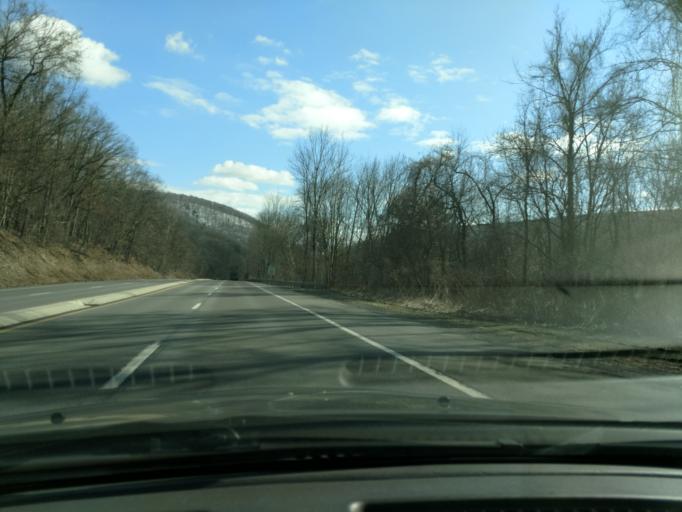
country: US
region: Pennsylvania
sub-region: Berks County
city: West Hamburg
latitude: 40.5890
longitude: -76.0270
